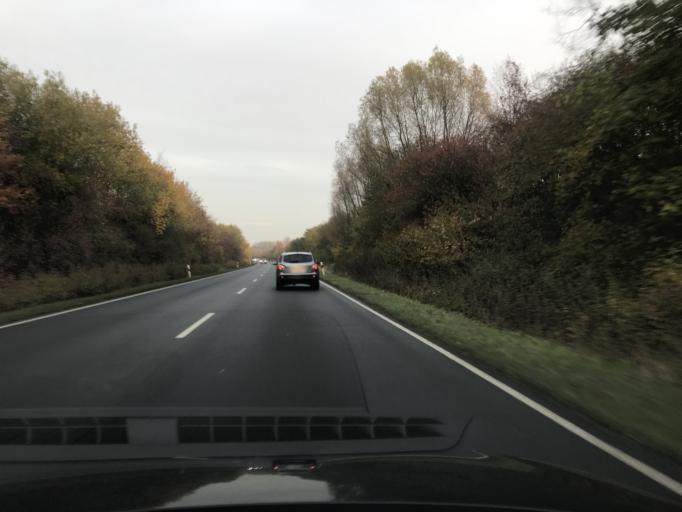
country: DE
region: North Rhine-Westphalia
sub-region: Regierungsbezirk Arnsberg
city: Hamm
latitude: 51.7052
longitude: 7.7373
